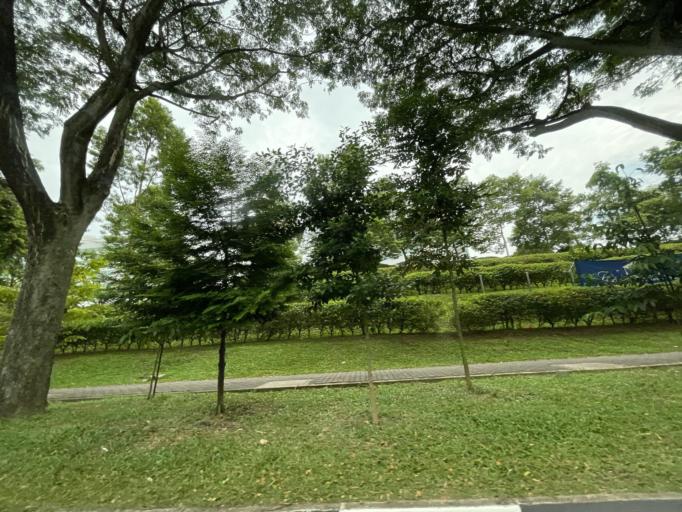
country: SG
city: Singapore
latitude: 1.3012
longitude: 103.7712
